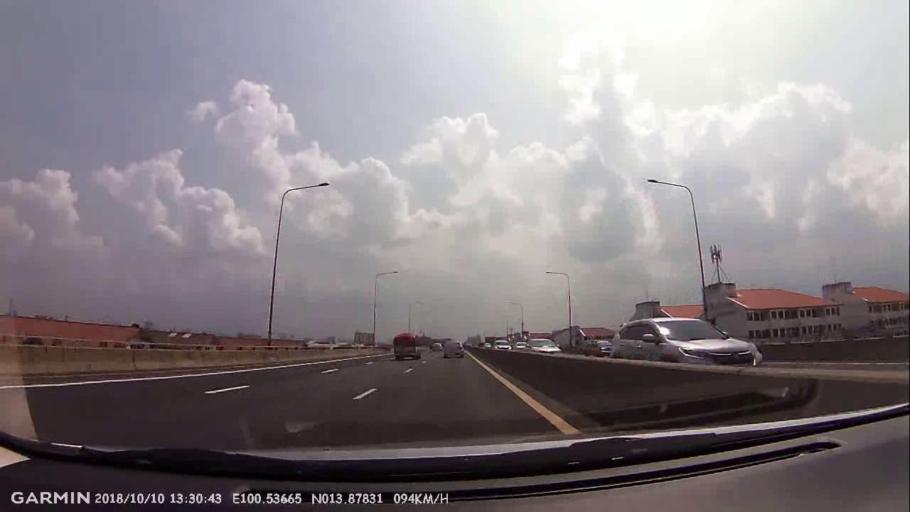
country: TH
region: Nonthaburi
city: Mueang Nonthaburi
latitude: 13.8781
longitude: 100.5366
